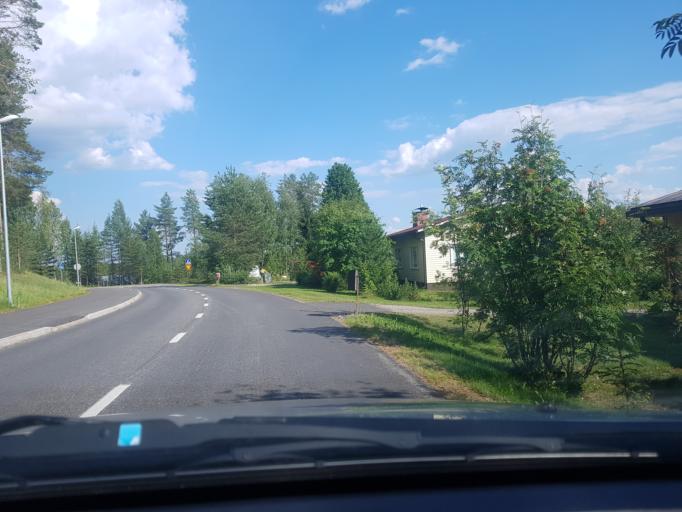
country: FI
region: Kainuu
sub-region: Kehys-Kainuu
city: Kuhmo
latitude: 64.1275
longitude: 29.5394
